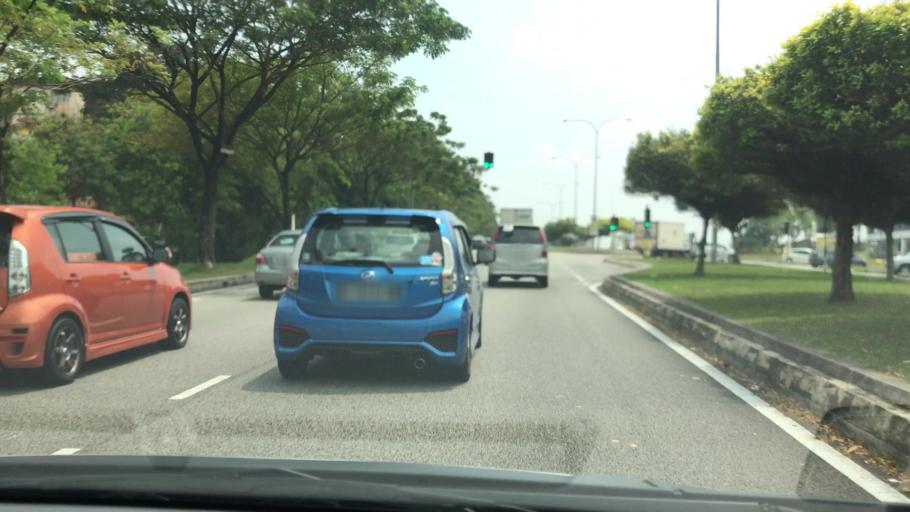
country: MY
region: Putrajaya
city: Putrajaya
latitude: 2.9979
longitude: 101.6649
